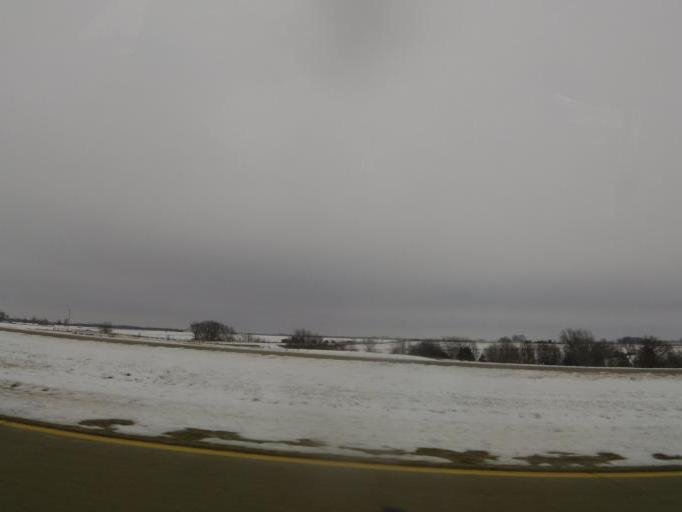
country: US
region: Illinois
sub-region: Hancock County
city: Nauvoo
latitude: 40.6088
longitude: -91.5608
